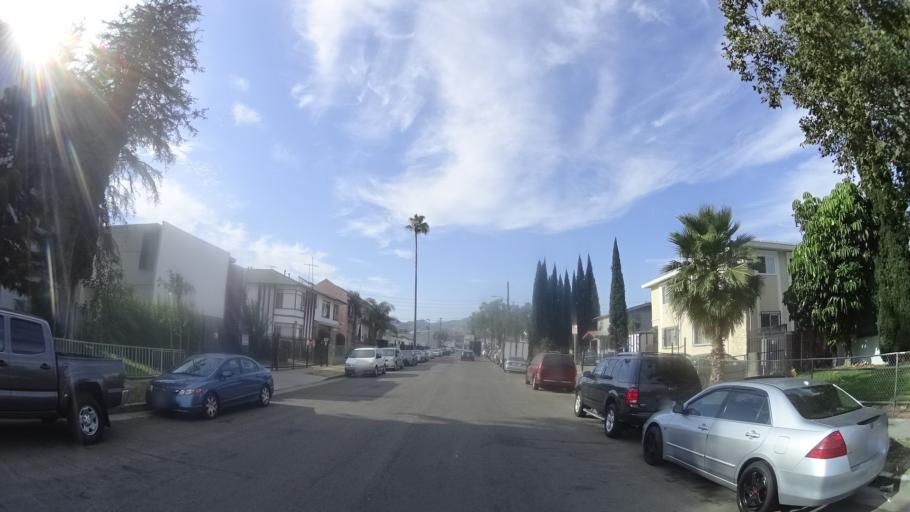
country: US
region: California
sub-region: Los Angeles County
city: Hollywood
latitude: 34.0891
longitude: -118.3019
